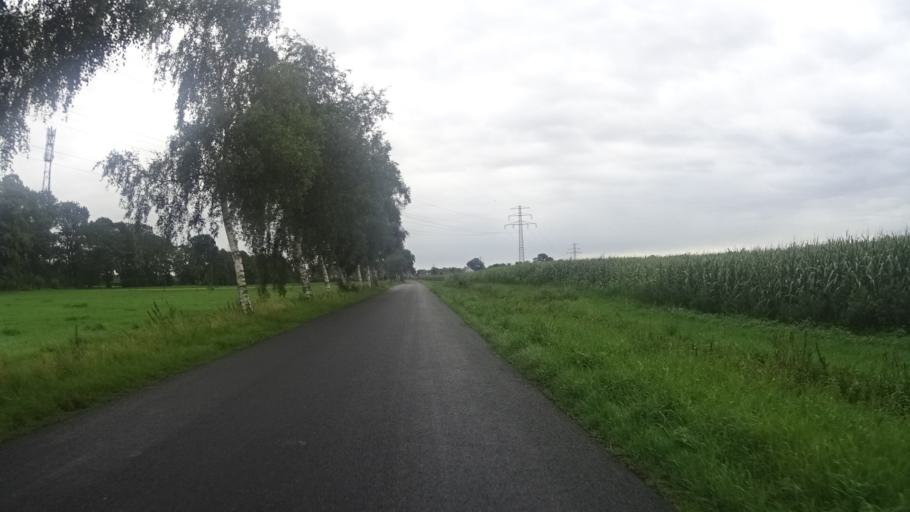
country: DE
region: Schleswig-Holstein
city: Kiebitzreihe
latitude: 53.7870
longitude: 9.6051
